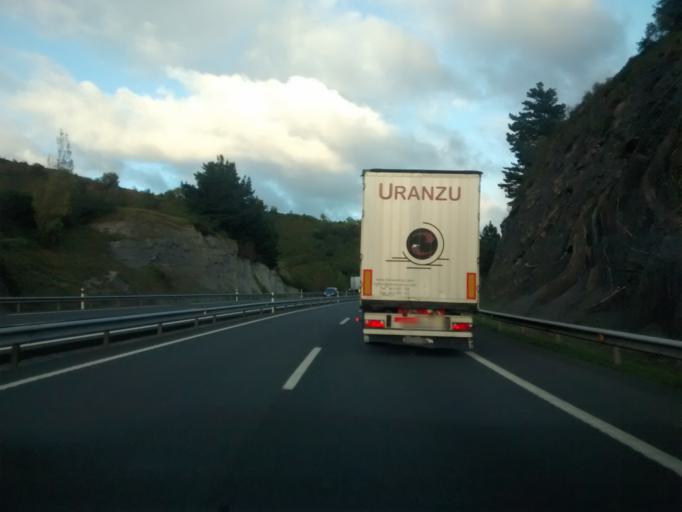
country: ES
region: Basque Country
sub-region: Provincia de Guipuzcoa
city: Zumaia
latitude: 43.2711
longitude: -2.2654
